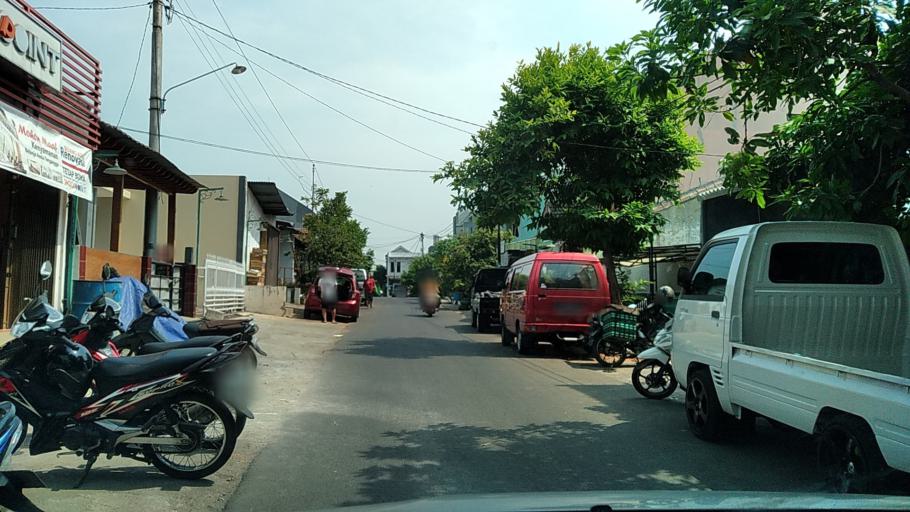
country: ID
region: Central Java
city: Ungaran
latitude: -7.0695
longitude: 110.4170
